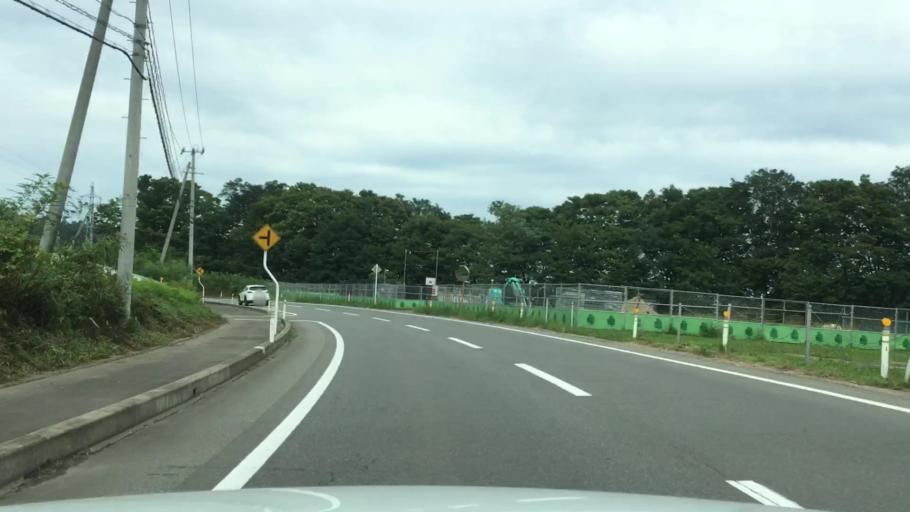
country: JP
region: Aomori
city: Shimokizukuri
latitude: 40.7663
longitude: 140.2244
